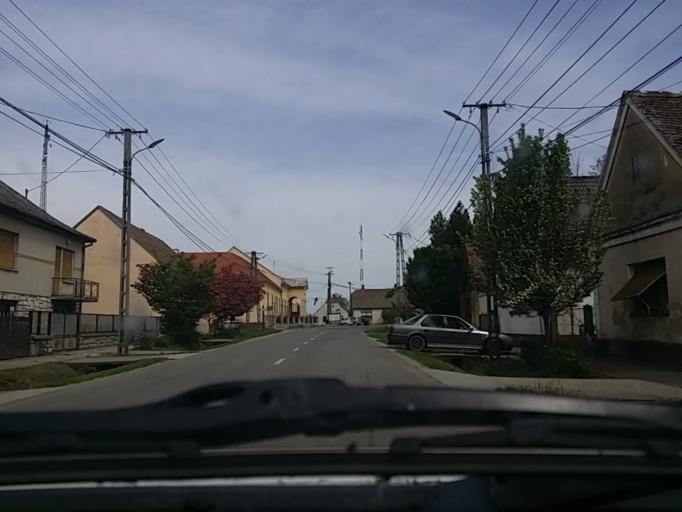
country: HU
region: Baranya
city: Sellye
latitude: 45.8740
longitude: 17.8427
